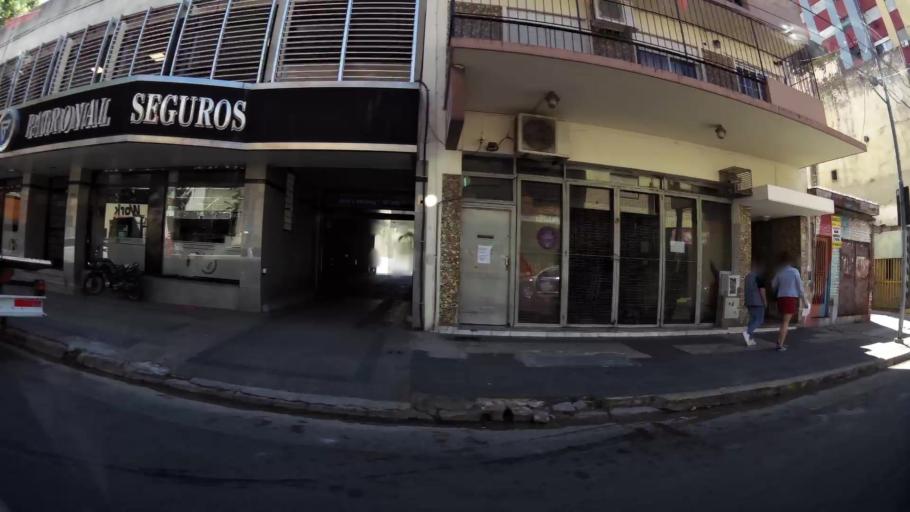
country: AR
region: Buenos Aires
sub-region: Partido de General San Martin
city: General San Martin
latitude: -34.5748
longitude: -58.5397
